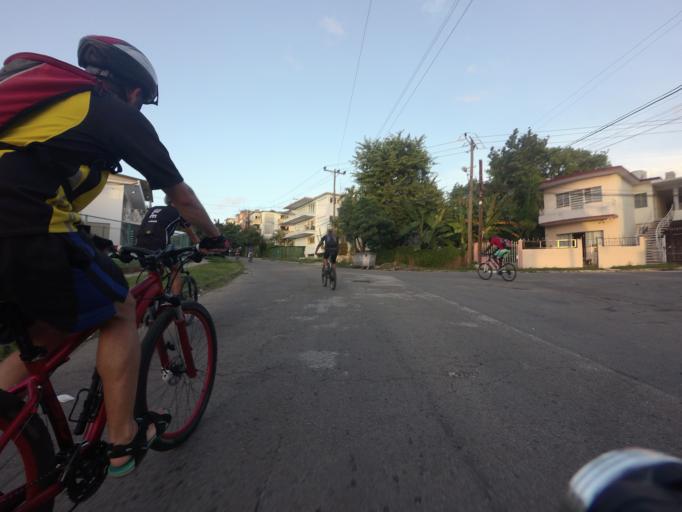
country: CU
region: La Habana
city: Havana
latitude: 23.1163
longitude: -82.4029
